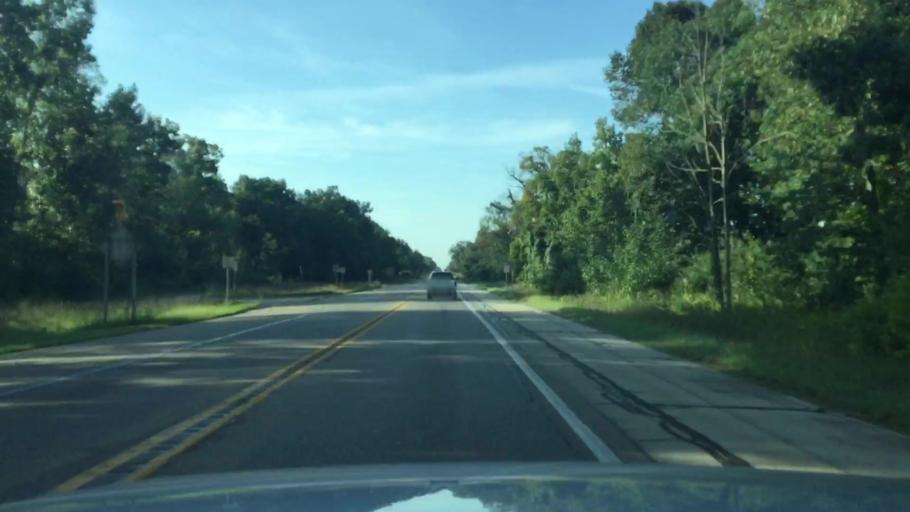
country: US
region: Michigan
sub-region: Jackson County
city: Vandercook Lake
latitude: 42.1153
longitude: -84.3641
